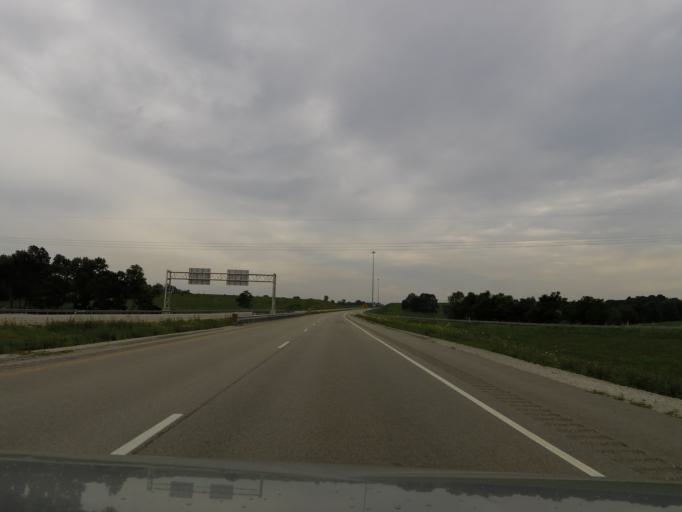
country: US
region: Ohio
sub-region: Brown County
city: Aberdeen
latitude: 38.6392
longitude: -83.8324
